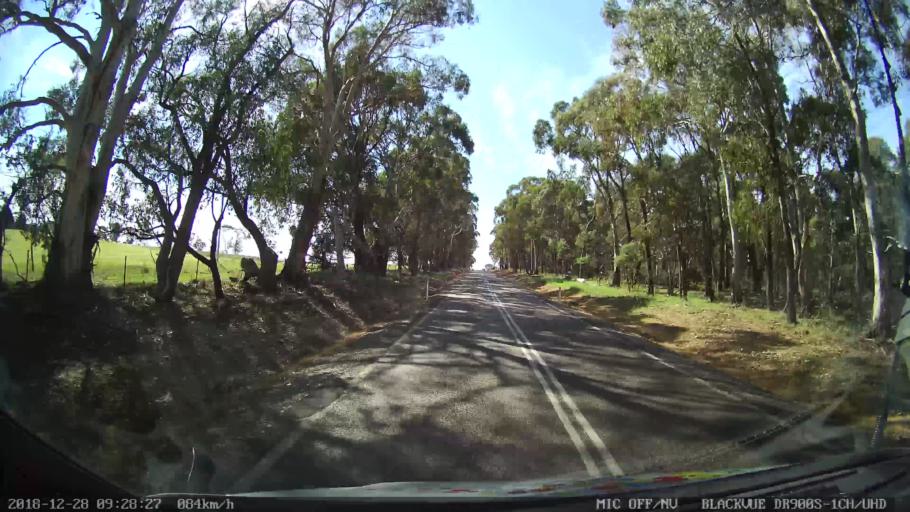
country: AU
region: New South Wales
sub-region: Upper Lachlan Shire
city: Crookwell
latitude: -34.4391
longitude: 149.4163
